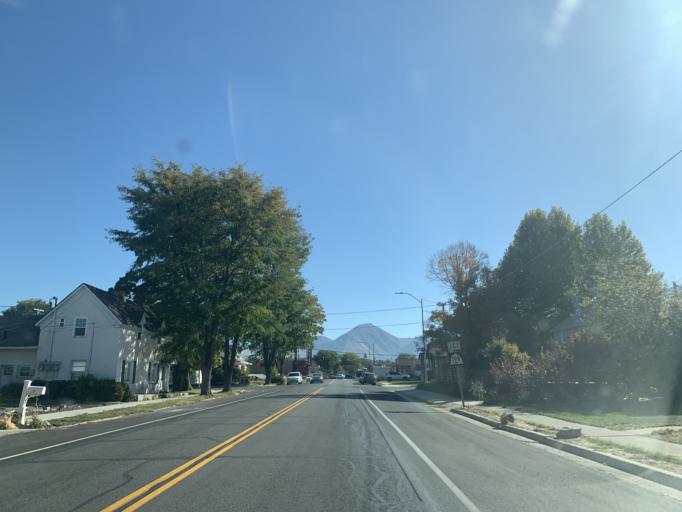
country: US
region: Utah
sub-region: Utah County
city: Payson
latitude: 40.0436
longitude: -111.7359
